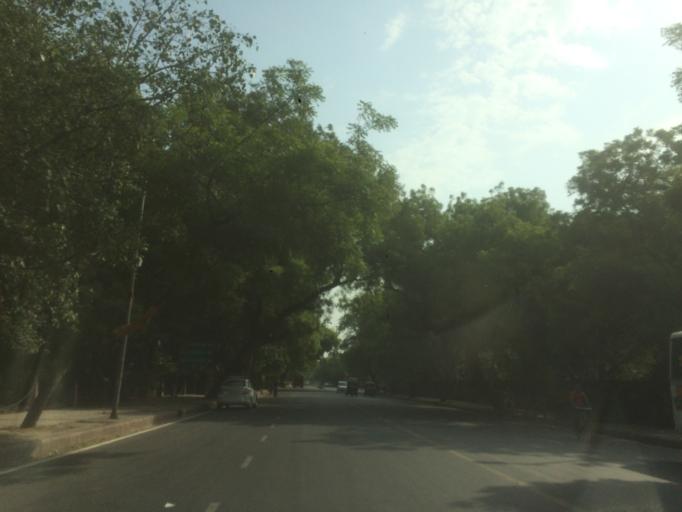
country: IN
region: NCT
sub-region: New Delhi
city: New Delhi
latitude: 28.6256
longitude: 77.2143
